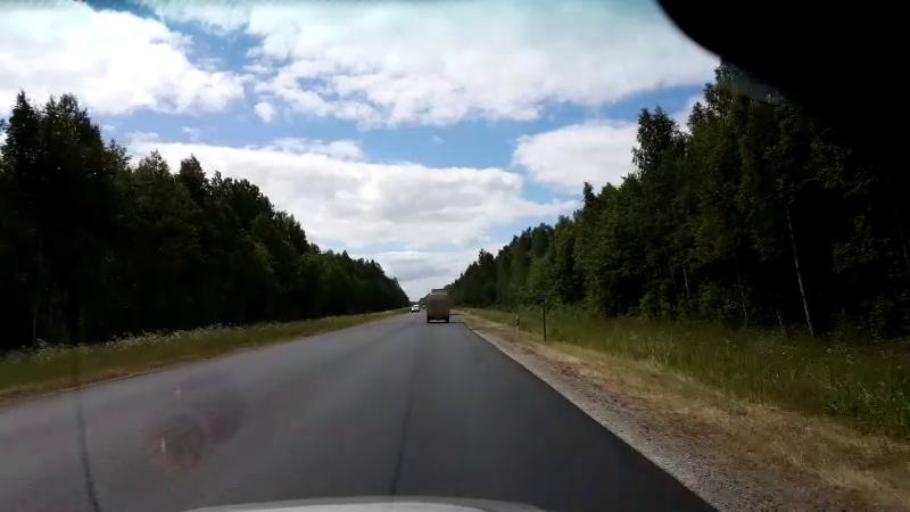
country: LV
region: Salacgrivas
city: Ainazi
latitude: 57.9341
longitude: 24.4281
